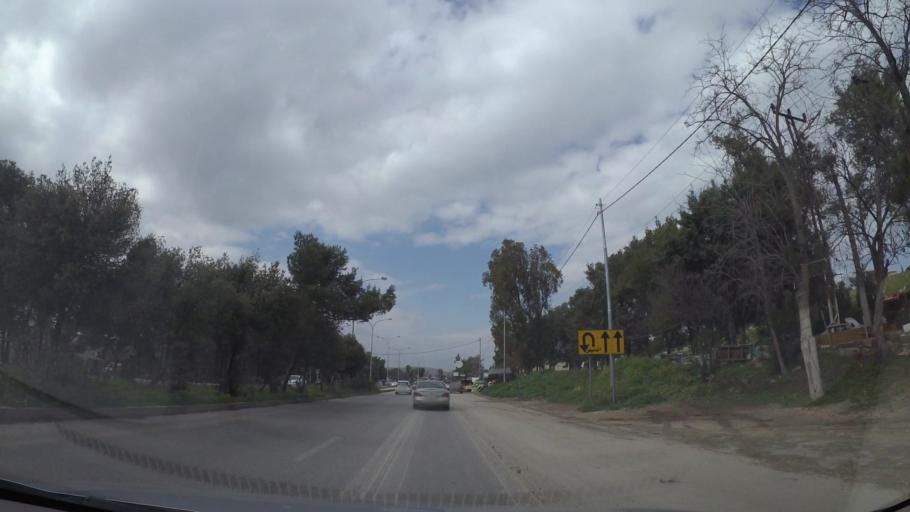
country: JO
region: Balqa
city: As Salt
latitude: 32.0366
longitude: 35.7906
